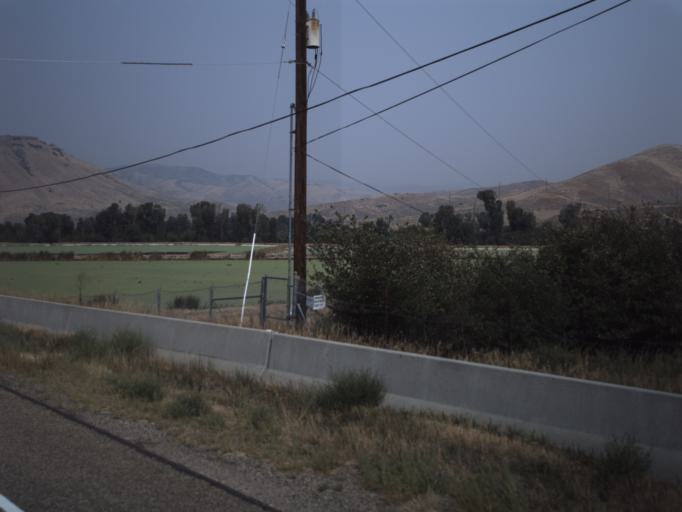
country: US
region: Utah
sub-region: Summit County
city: Coalville
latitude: 41.0283
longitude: -111.5080
